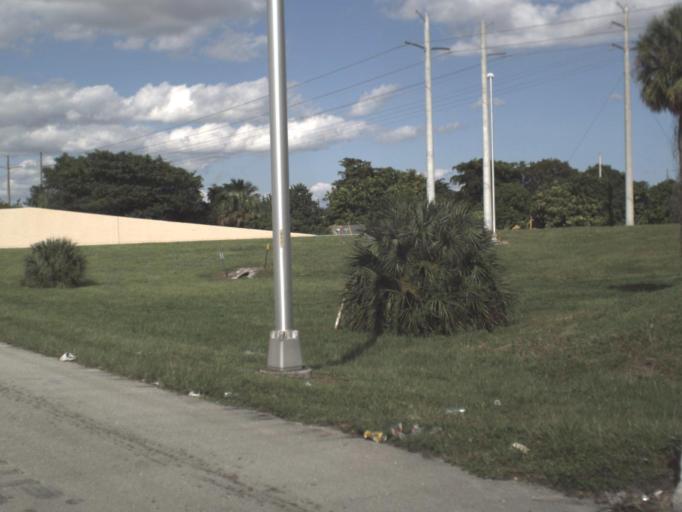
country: US
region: Florida
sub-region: Broward County
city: Lauderhill
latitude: 26.1400
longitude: -80.2190
